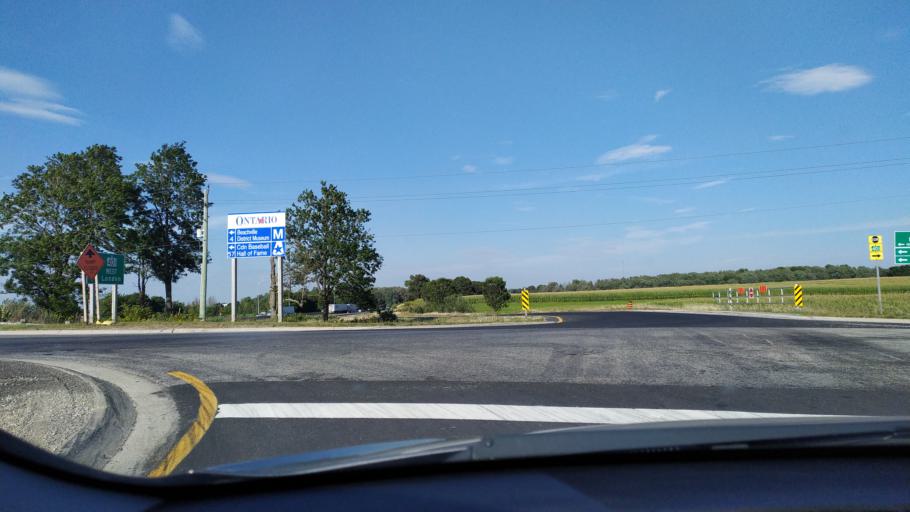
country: CA
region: Ontario
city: Ingersoll
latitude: 43.0497
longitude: -80.8209
